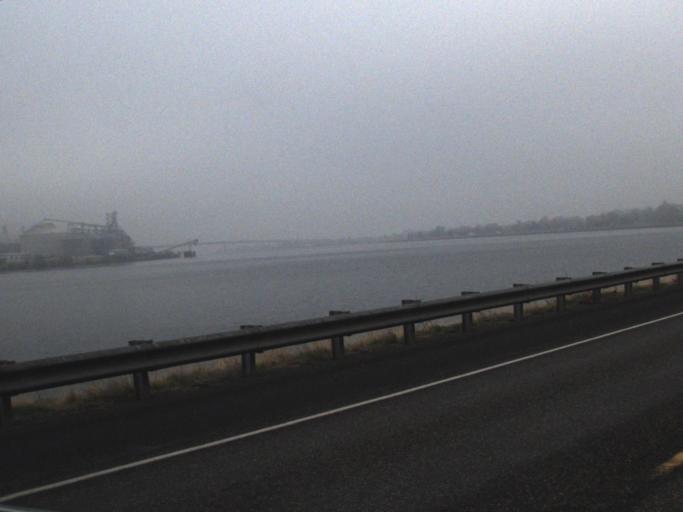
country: US
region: Washington
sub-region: Asotin County
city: Clarkston Heights-Vineland
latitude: 46.4162
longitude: -117.0997
